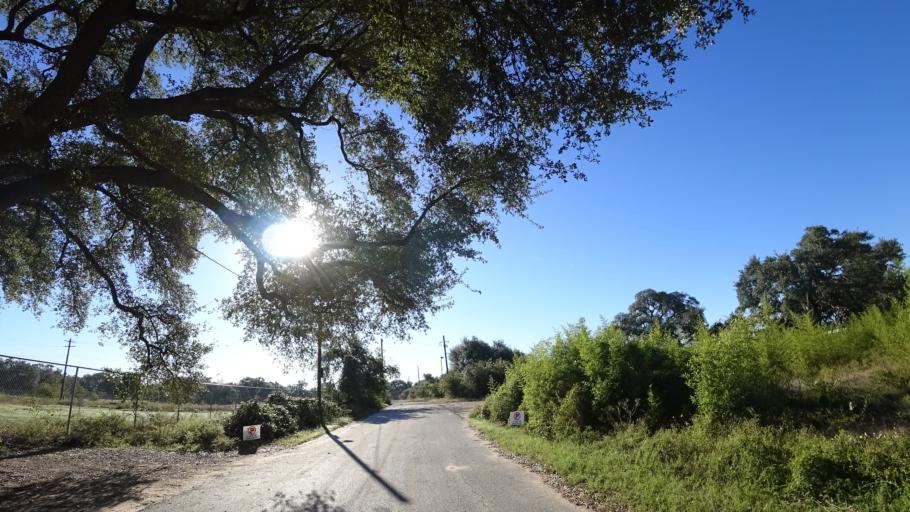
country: US
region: Texas
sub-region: Travis County
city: Hornsby Bend
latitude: 30.2201
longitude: -97.6611
